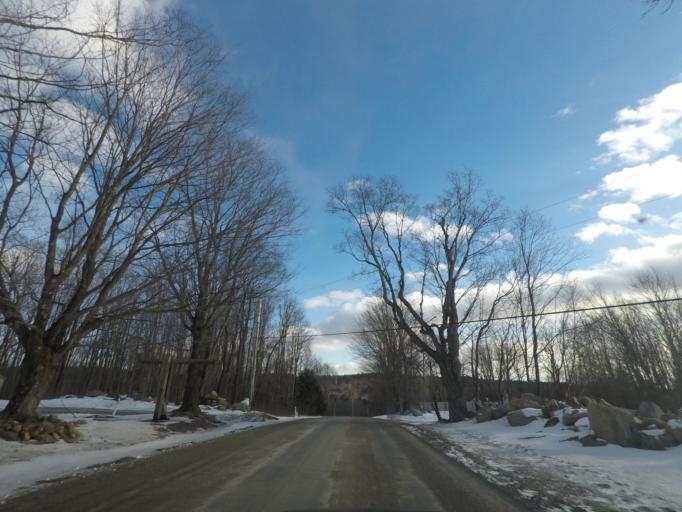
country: US
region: New York
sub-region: Rensselaer County
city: Poestenkill
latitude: 42.7402
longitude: -73.4727
